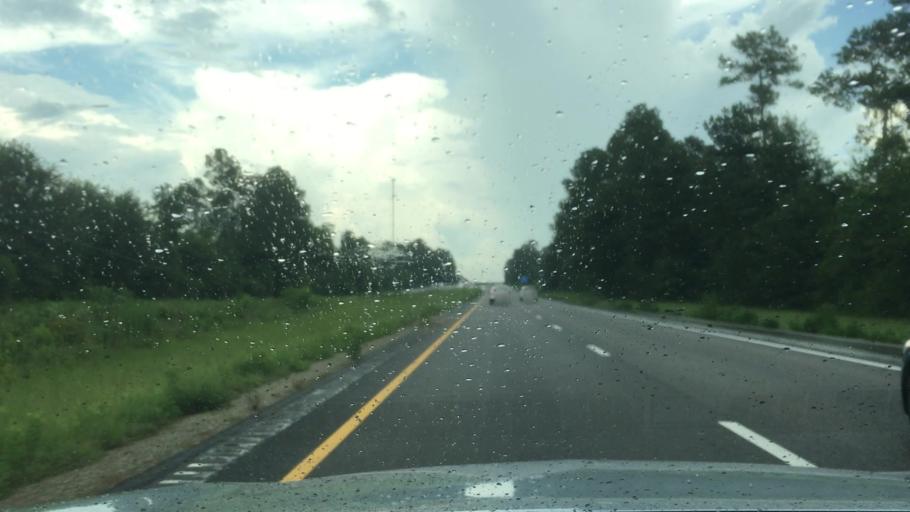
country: US
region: Mississippi
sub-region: Lamar County
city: Purvis
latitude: 31.1804
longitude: -89.3459
